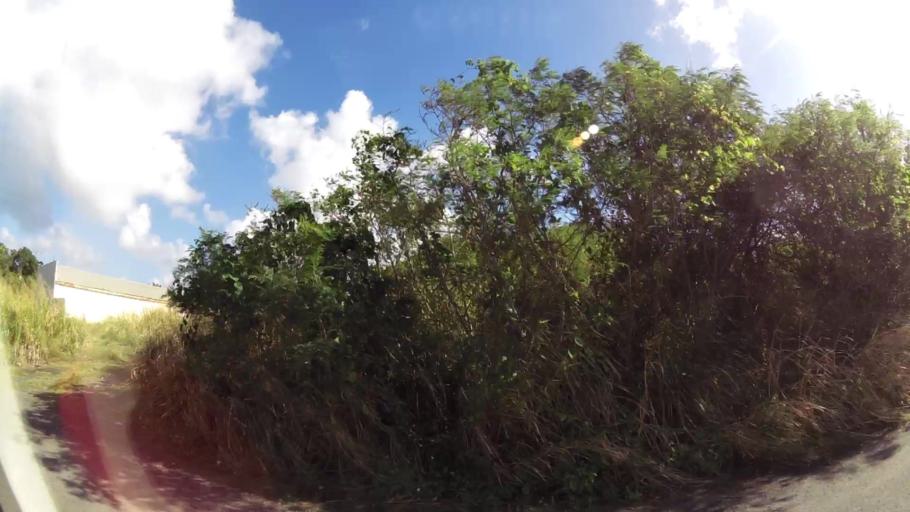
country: LC
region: Castries Quarter
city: Bisee
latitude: 14.0183
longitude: -60.9976
